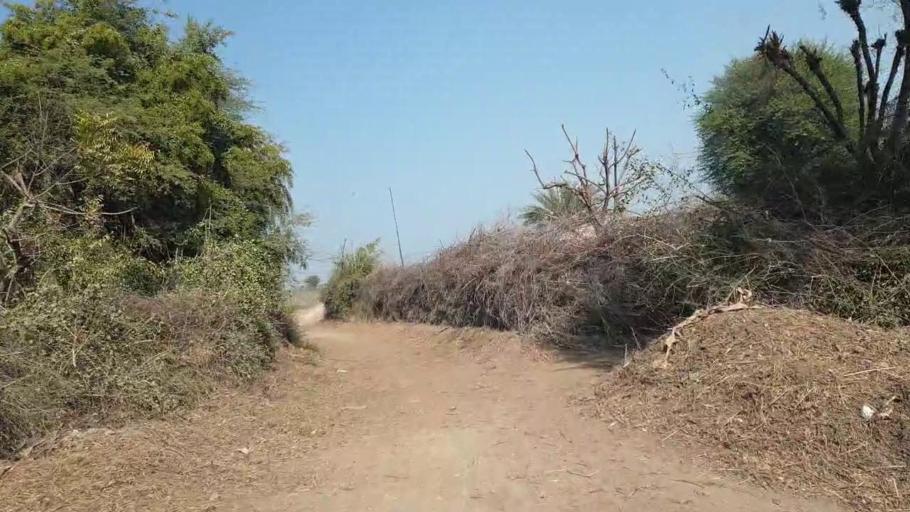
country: PK
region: Sindh
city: Hala
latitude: 25.9444
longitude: 68.4443
